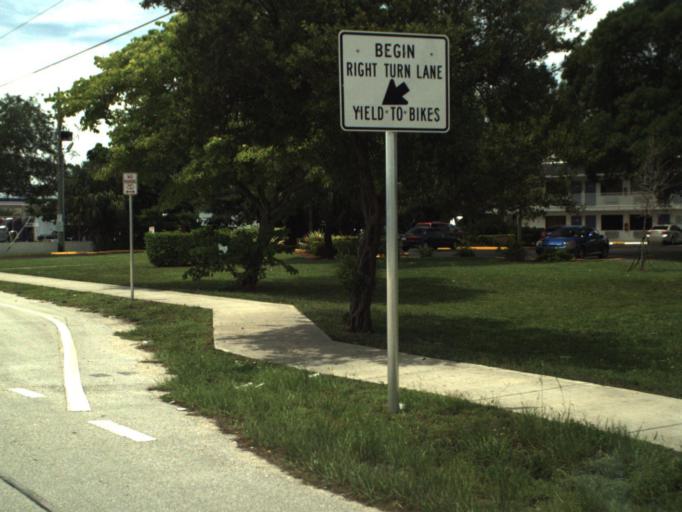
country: US
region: Florida
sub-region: Broward County
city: Coconut Creek
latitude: 26.2431
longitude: -80.1651
